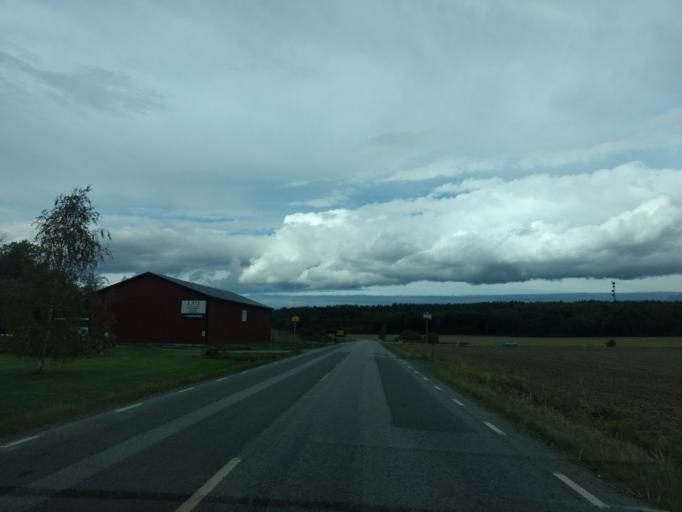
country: SE
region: Uppsala
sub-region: Habo Kommun
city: Balsta
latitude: 59.6639
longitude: 17.5547
